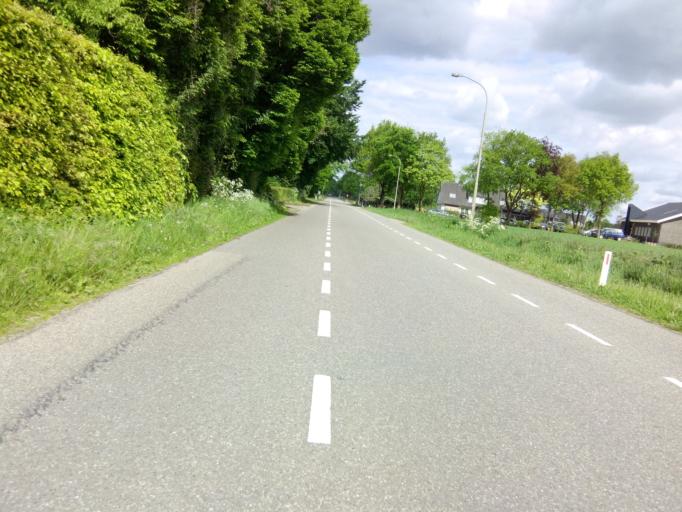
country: NL
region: Gelderland
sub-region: Gemeente Ede
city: Ede
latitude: 52.0740
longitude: 5.6784
